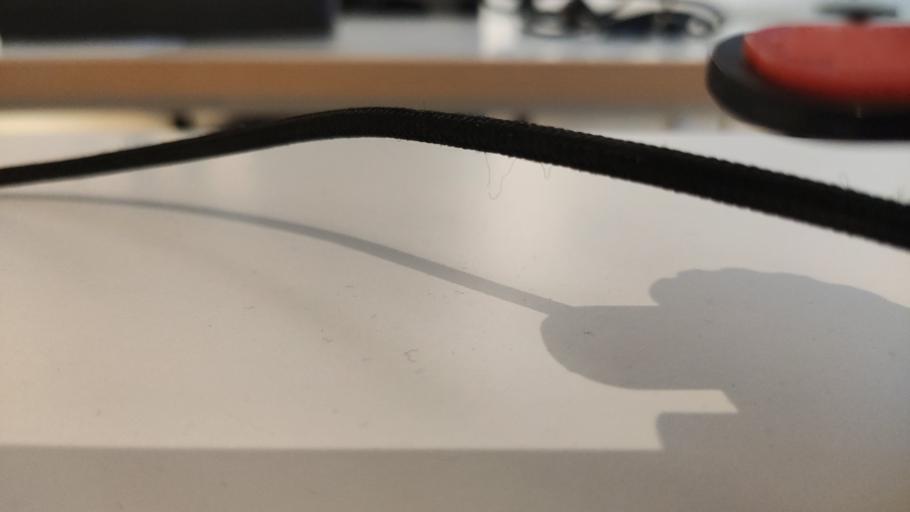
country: RU
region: Moskovskaya
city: Ruza
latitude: 55.7767
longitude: 36.2692
